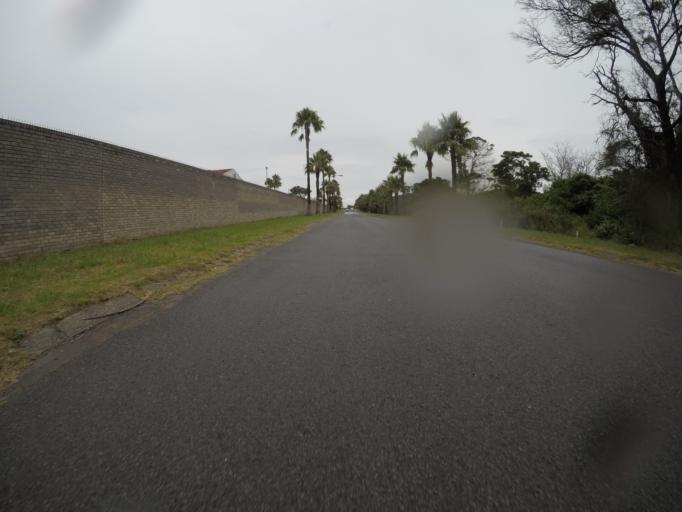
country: ZA
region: Eastern Cape
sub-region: Buffalo City Metropolitan Municipality
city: East London
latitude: -32.9712
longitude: 27.8187
